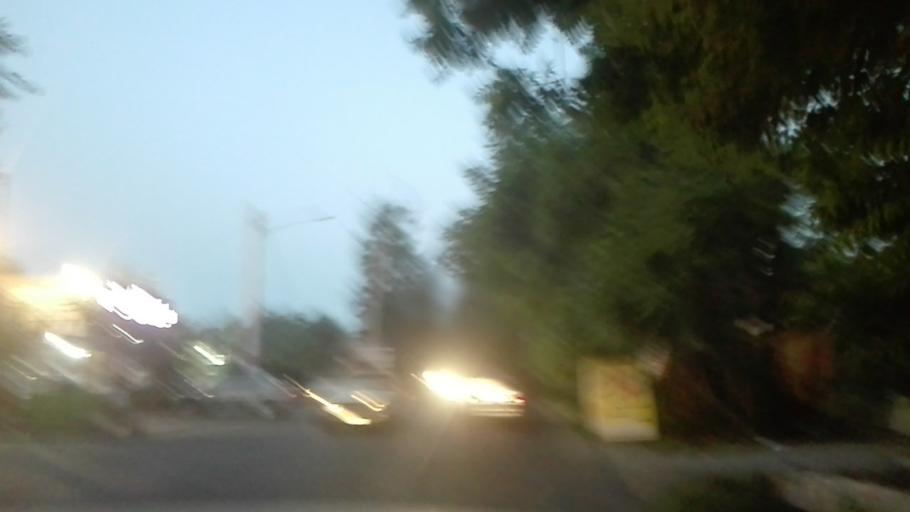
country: IR
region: Tehran
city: Shahriar
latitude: 35.6459
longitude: 51.0551
